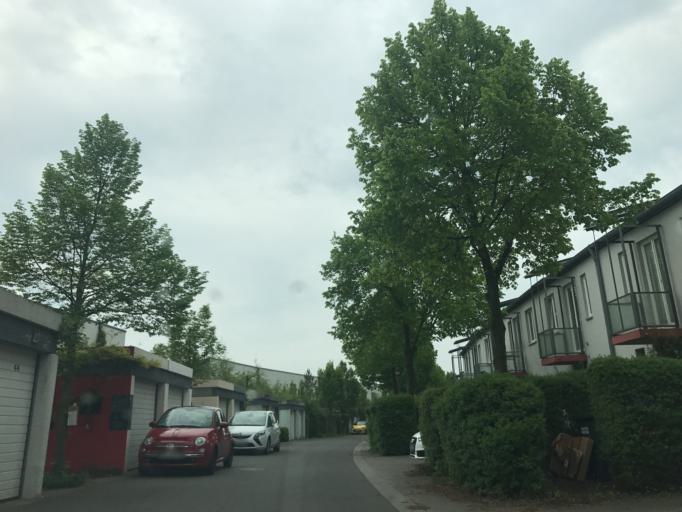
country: DE
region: Berlin
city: Staaken
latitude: 52.5597
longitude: 13.1402
